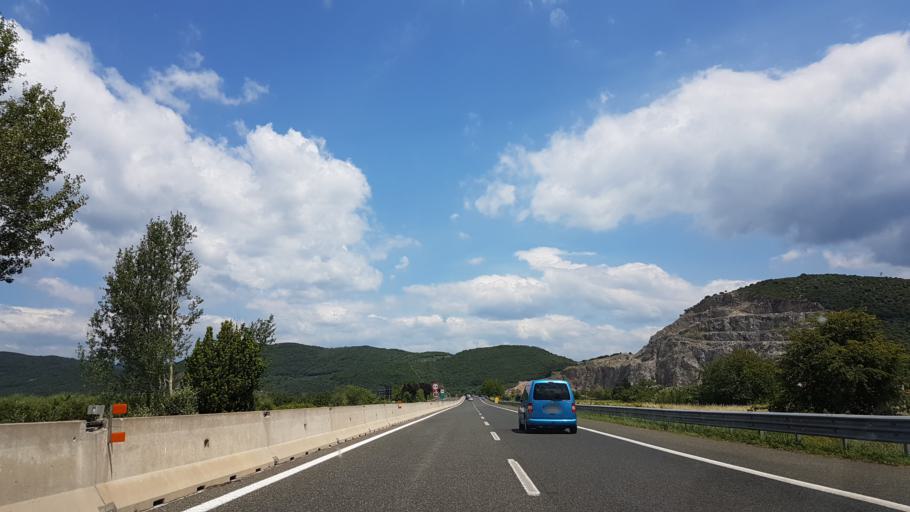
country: IT
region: Tuscany
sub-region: Province of Pisa
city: Vecchiano-Nodica
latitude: 43.7991
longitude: 10.3628
